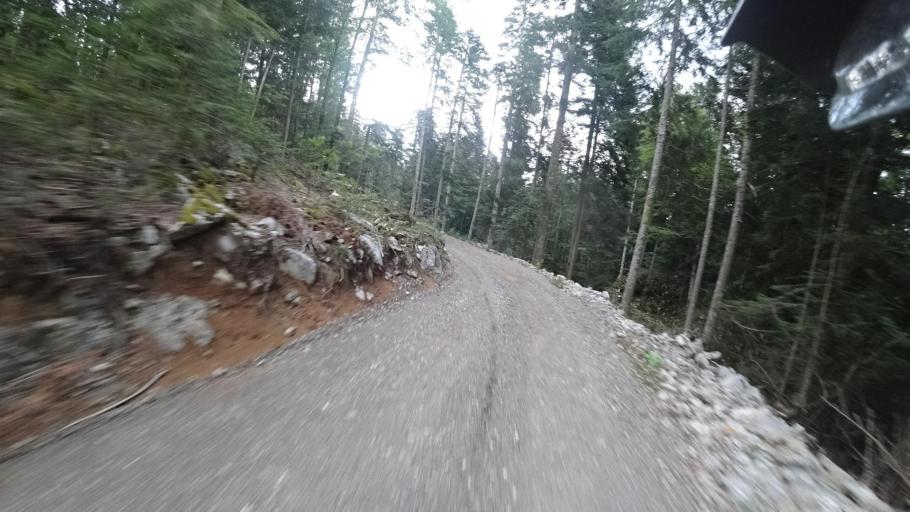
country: HR
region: Licko-Senjska
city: Senj
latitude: 45.1168
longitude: 14.9726
